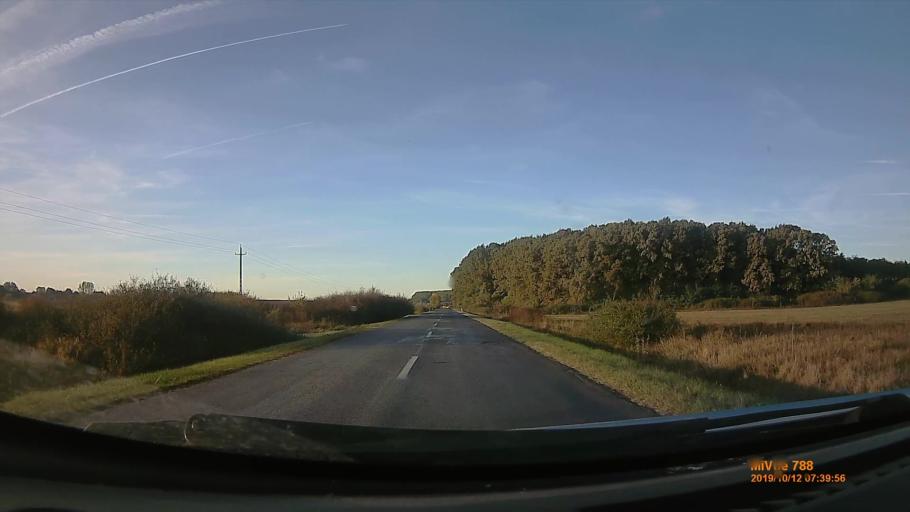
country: HU
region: Hajdu-Bihar
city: Pocsaj
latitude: 47.2097
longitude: 21.7996
